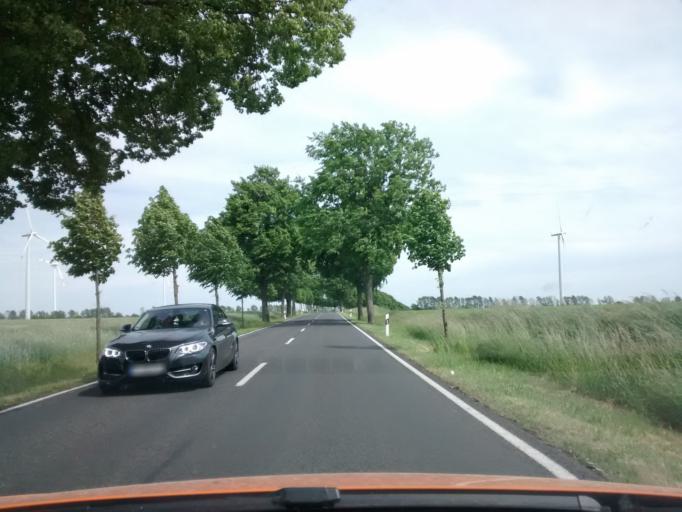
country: DE
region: Brandenburg
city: Ihlow
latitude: 51.8892
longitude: 13.3126
